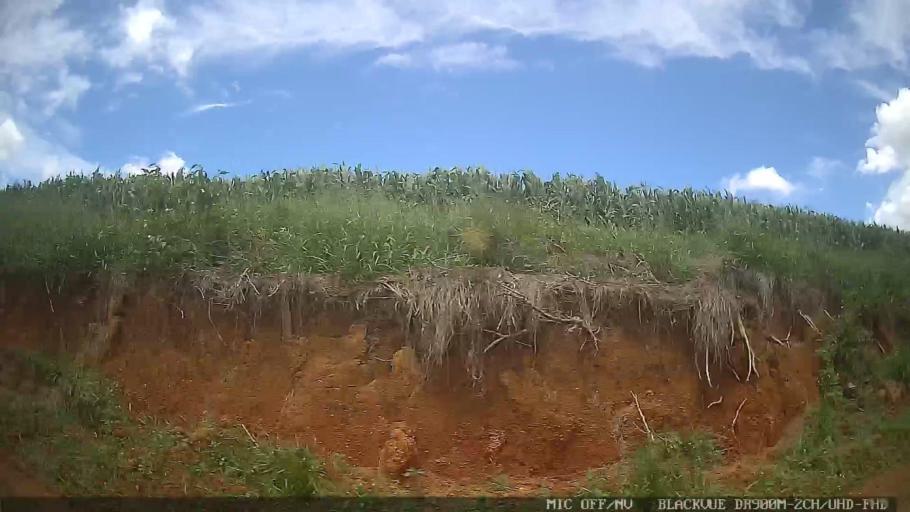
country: BR
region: Minas Gerais
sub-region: Extrema
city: Extrema
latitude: -22.7363
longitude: -46.4293
